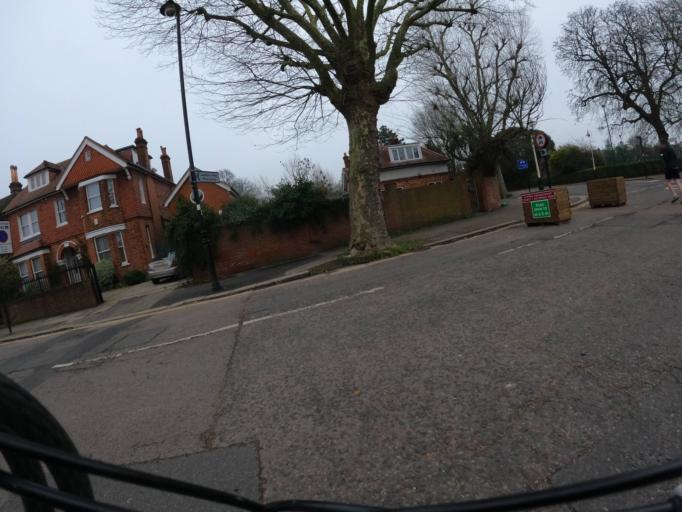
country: GB
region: England
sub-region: Greater London
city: Ealing
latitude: 51.5066
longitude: -0.3108
